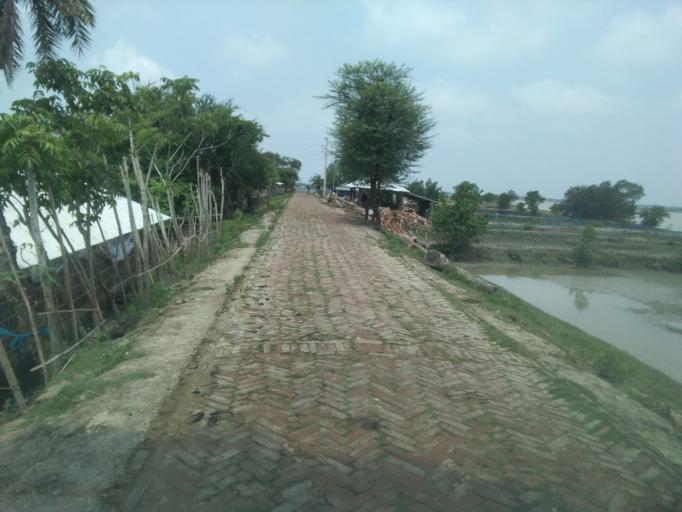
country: BD
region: Khulna
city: Phultala
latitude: 22.6422
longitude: 89.4205
